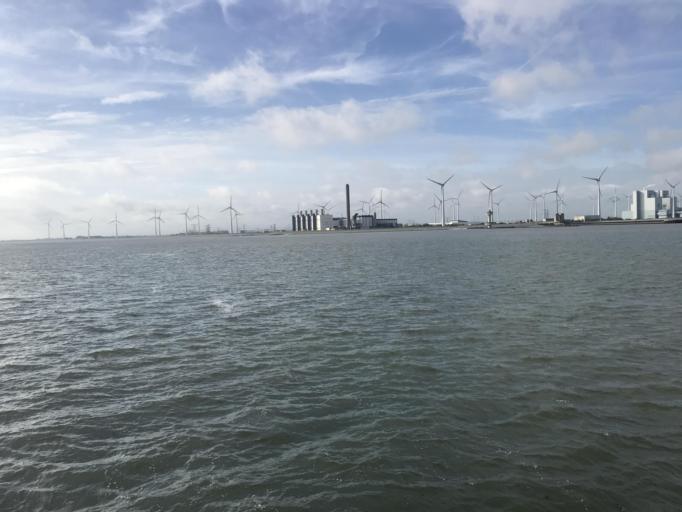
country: NL
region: Groningen
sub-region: Gemeente Delfzijl
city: Delfzijl
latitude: 53.4450
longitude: 6.8980
